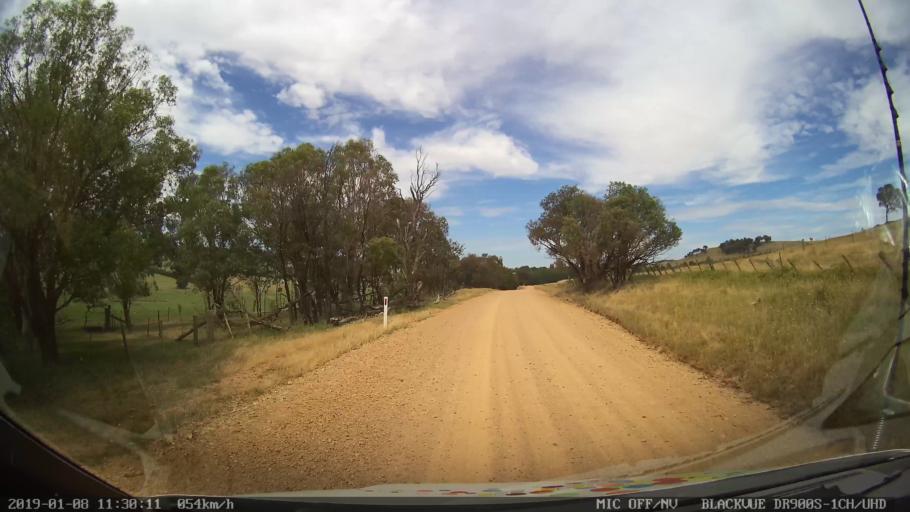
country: AU
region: New South Wales
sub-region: Guyra
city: Guyra
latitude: -30.3062
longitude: 151.5456
